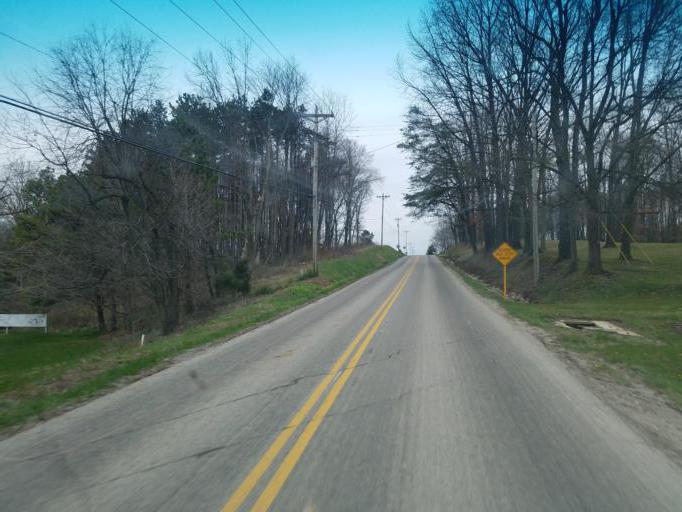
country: US
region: Ohio
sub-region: Holmes County
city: Millersburg
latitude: 40.6425
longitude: -81.9239
